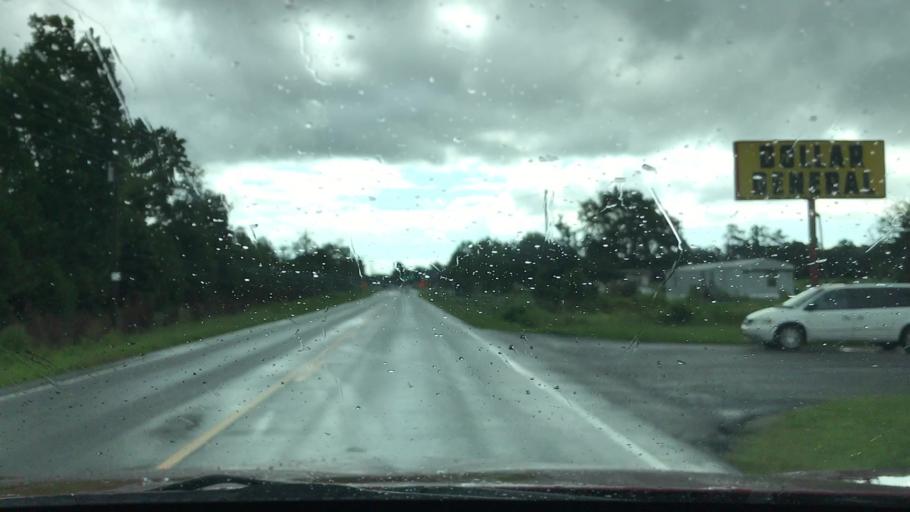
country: US
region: South Carolina
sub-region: Horry County
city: Loris
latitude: 33.9050
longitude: -78.8446
